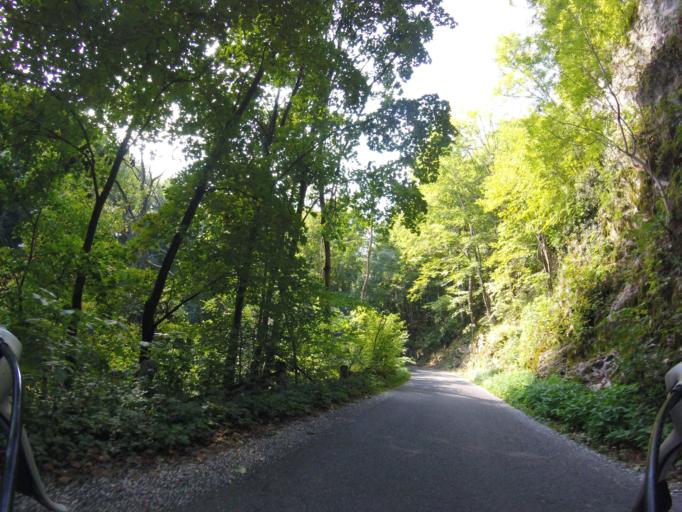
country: HU
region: Borsod-Abauj-Zemplen
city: Sajobabony
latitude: 48.1116
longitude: 20.6058
